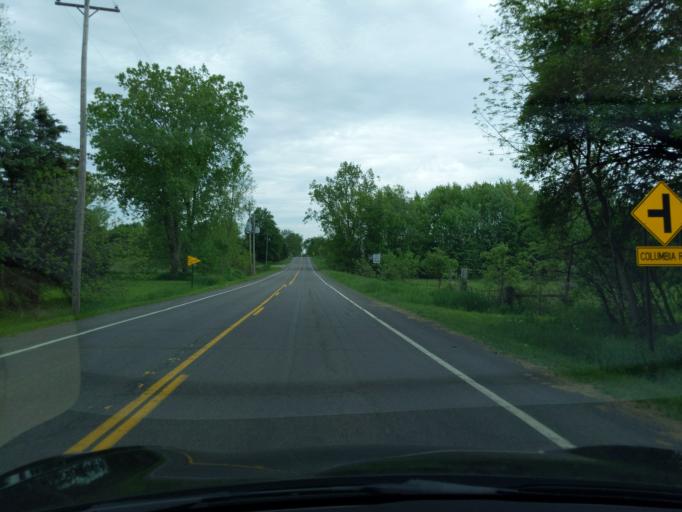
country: US
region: Michigan
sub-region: Ingham County
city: Mason
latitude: 42.5801
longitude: -84.3572
